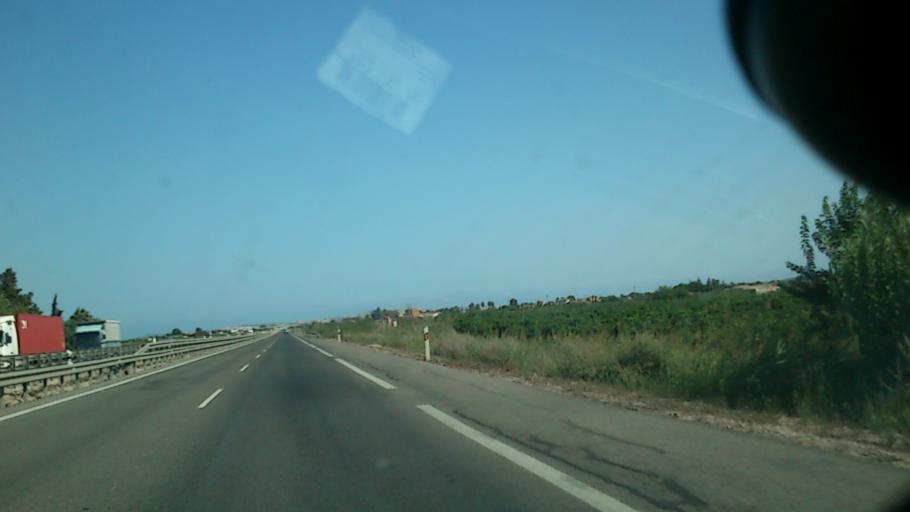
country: ES
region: Valencia
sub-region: Provincia de Alicante
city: Catral
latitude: 38.1419
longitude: -0.8108
